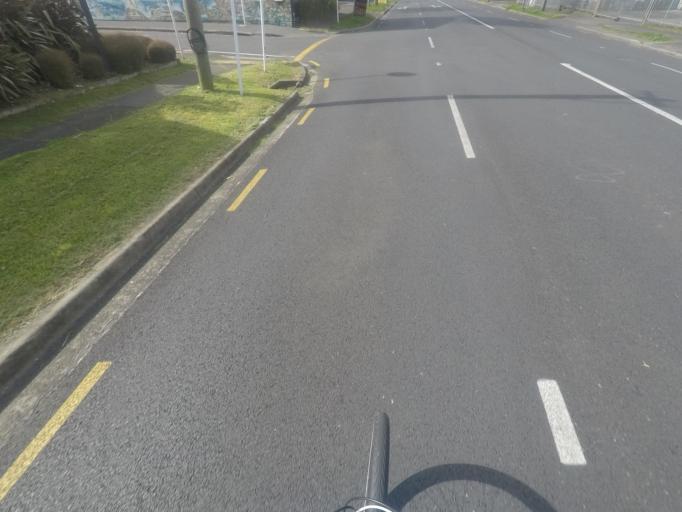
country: NZ
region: Auckland
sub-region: Auckland
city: Mangere
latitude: -36.9242
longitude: 174.7833
